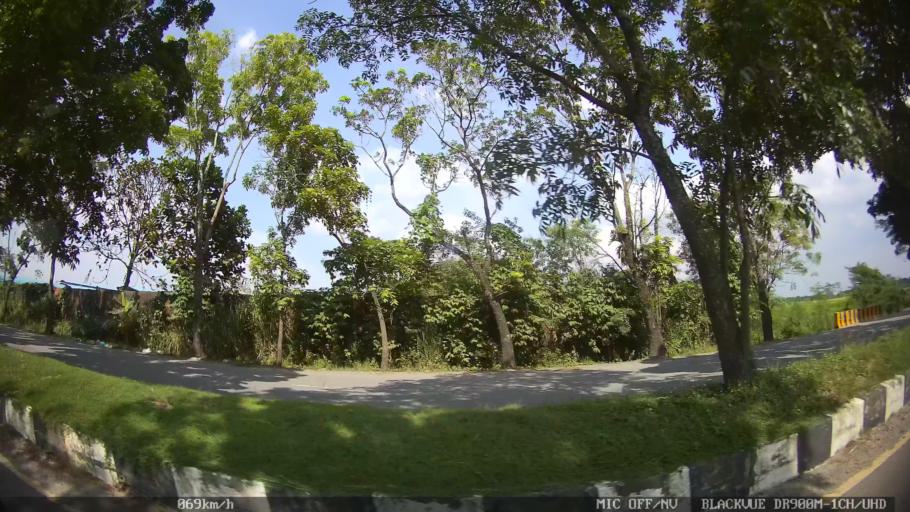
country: ID
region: North Sumatra
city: Binjai
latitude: 3.6274
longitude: 98.5350
